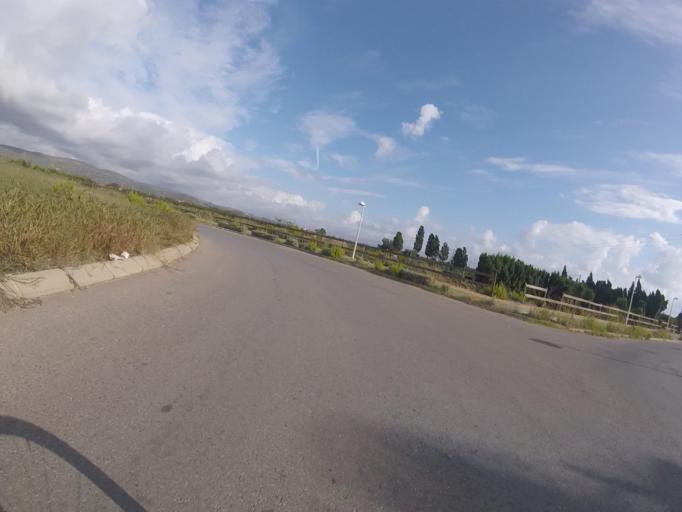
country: ES
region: Valencia
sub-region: Provincia de Castello
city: Orpesa/Oropesa del Mar
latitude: 40.1385
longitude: 0.1585
